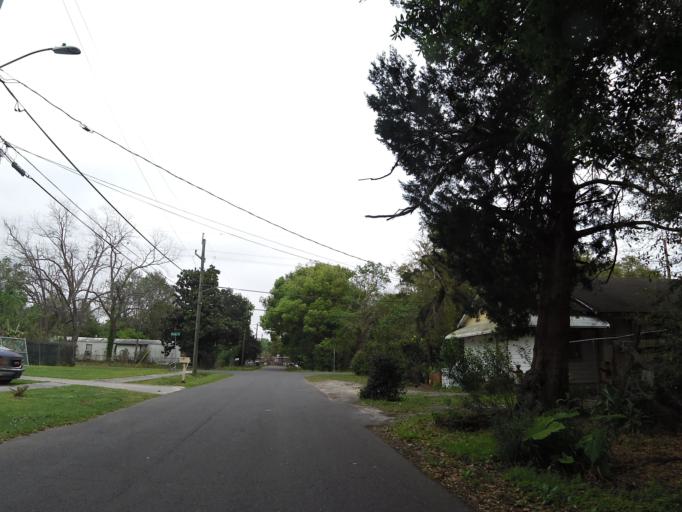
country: US
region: Florida
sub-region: Duval County
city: Jacksonville
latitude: 30.3232
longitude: -81.7247
